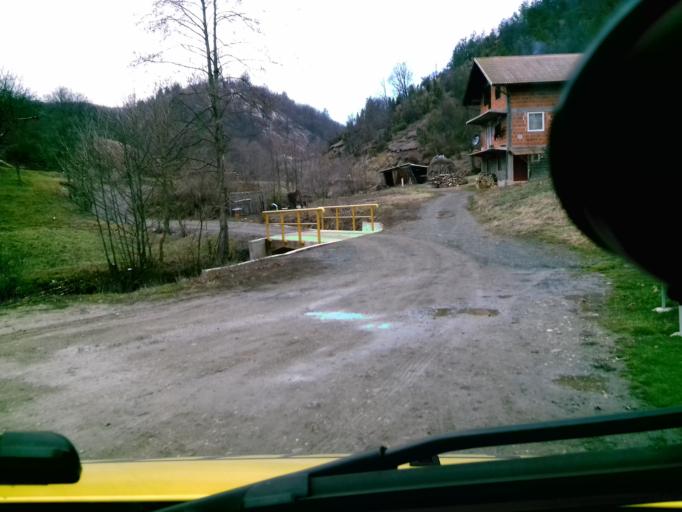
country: BA
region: Federation of Bosnia and Herzegovina
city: Zepce
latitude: 44.4673
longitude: 18.0271
